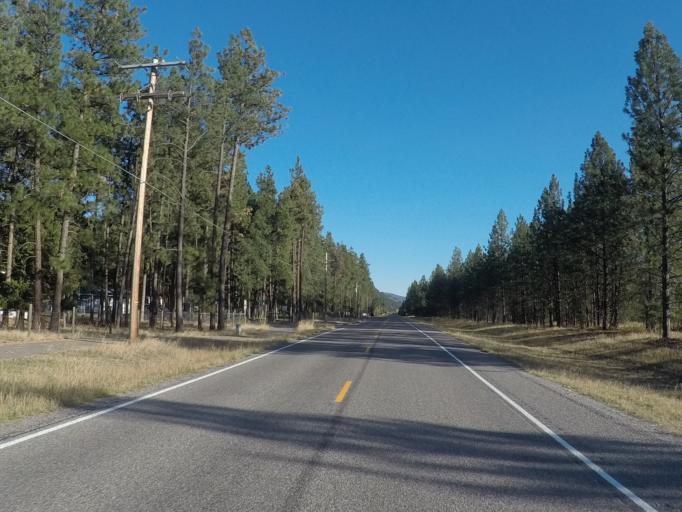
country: US
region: Montana
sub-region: Missoula County
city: Bonner-West Riverside
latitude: 46.8442
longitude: -113.8412
